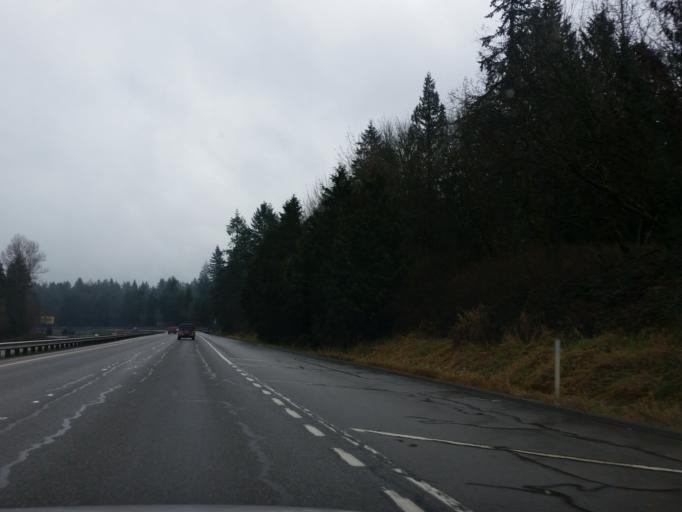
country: US
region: Washington
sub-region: Snohomish County
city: Maltby
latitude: 47.7948
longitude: -122.1235
